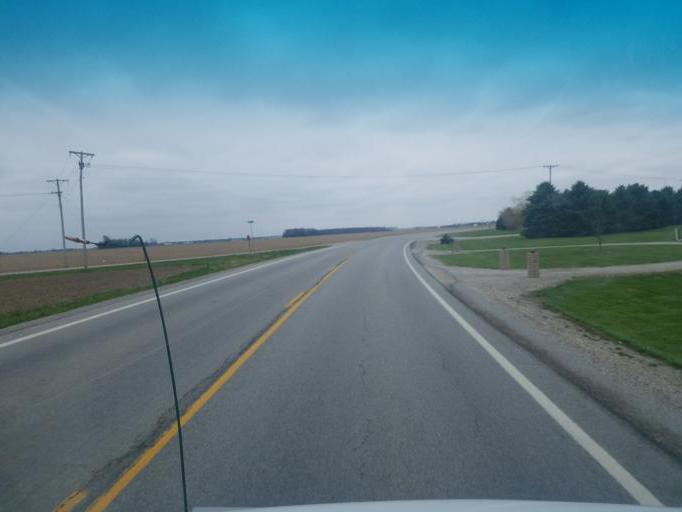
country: US
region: Ohio
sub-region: Van Wert County
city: Van Wert
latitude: 40.9178
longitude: -84.5476
